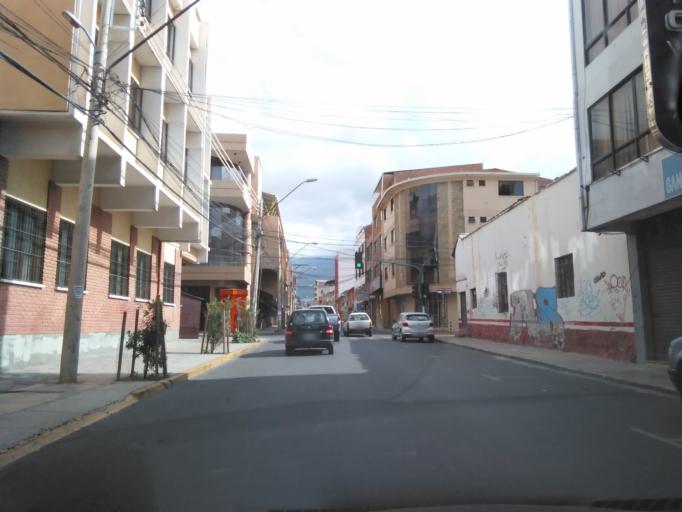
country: BO
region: Cochabamba
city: Cochabamba
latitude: -17.3906
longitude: -66.1525
